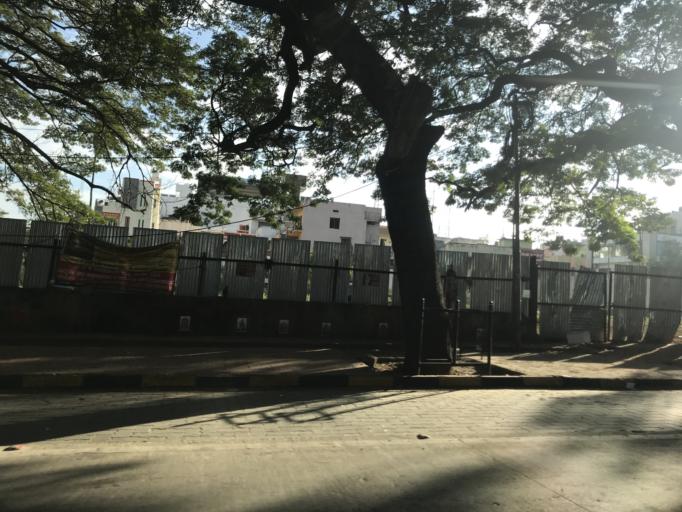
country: IN
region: Karnataka
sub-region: Mysore
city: Mysore
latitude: 12.3021
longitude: 76.6474
